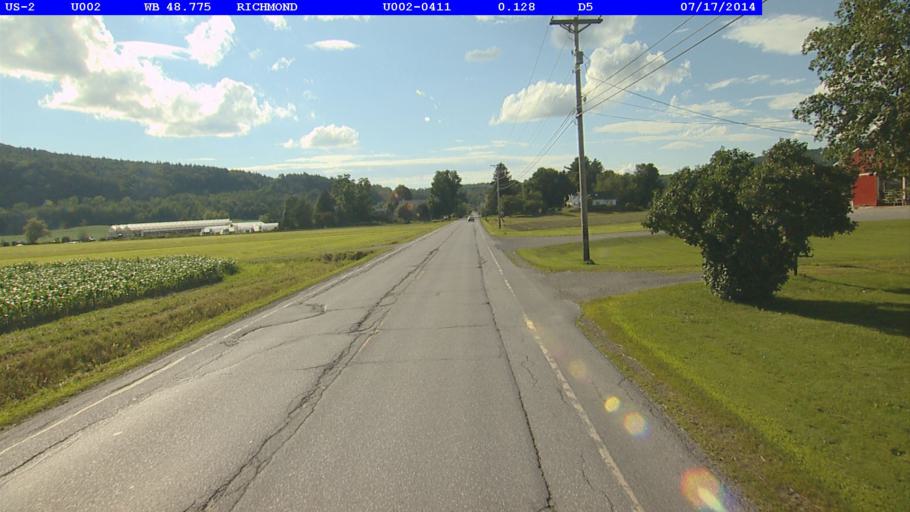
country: US
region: Vermont
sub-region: Chittenden County
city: Williston
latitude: 44.4279
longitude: -73.0263
